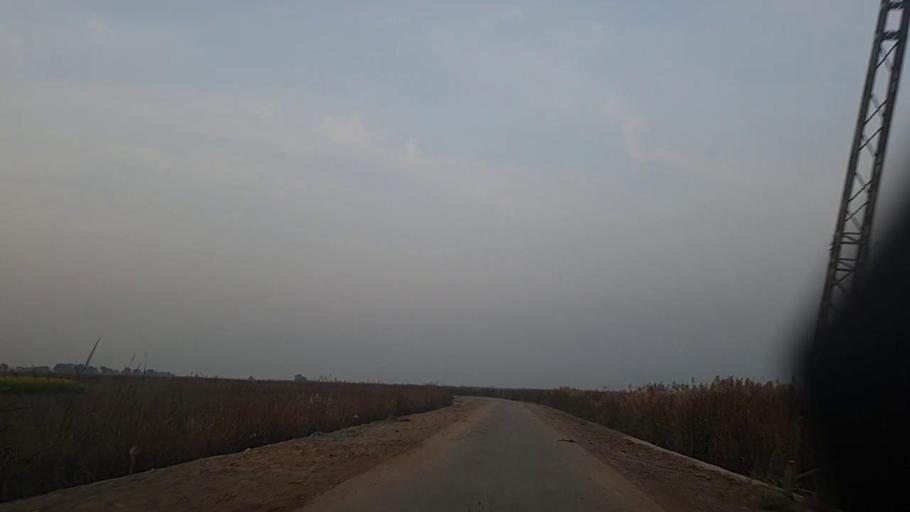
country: PK
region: Sindh
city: Sakrand
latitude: 26.0982
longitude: 68.3405
